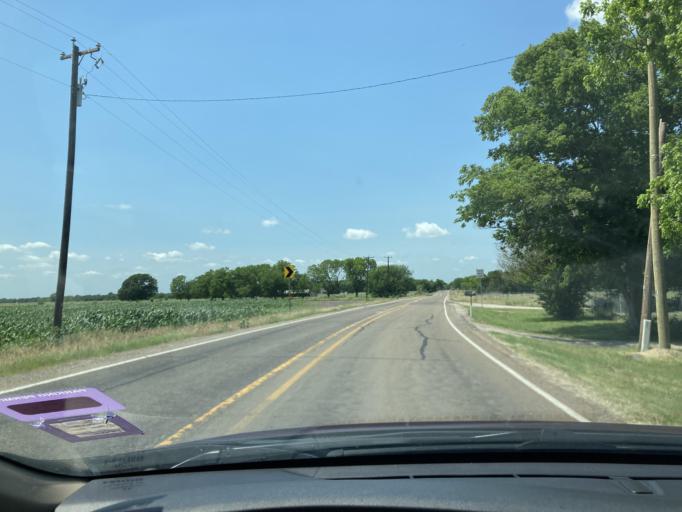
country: US
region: Texas
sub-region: Navarro County
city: Kerens
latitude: 32.1114
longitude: -96.3246
